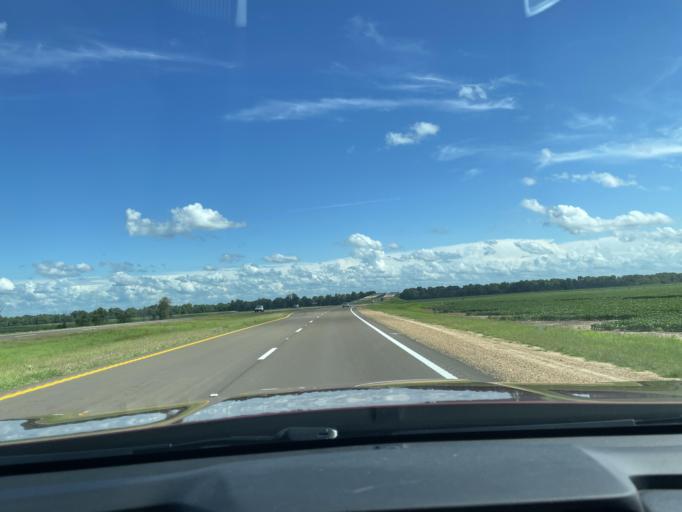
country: US
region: Mississippi
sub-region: Yazoo County
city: Yazoo City
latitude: 32.9390
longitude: -90.4136
